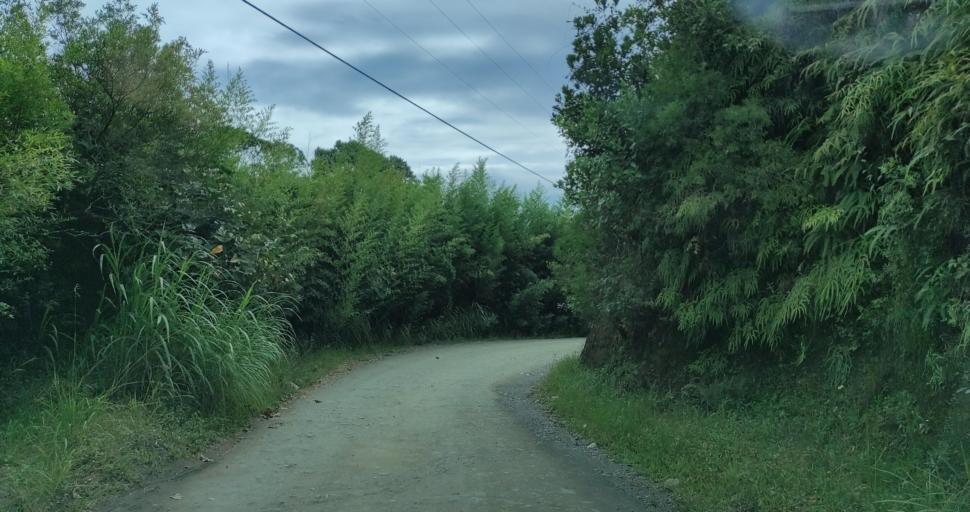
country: BR
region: Santa Catarina
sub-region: Porto Belo
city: Porto Belo
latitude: -27.2116
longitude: -48.5012
